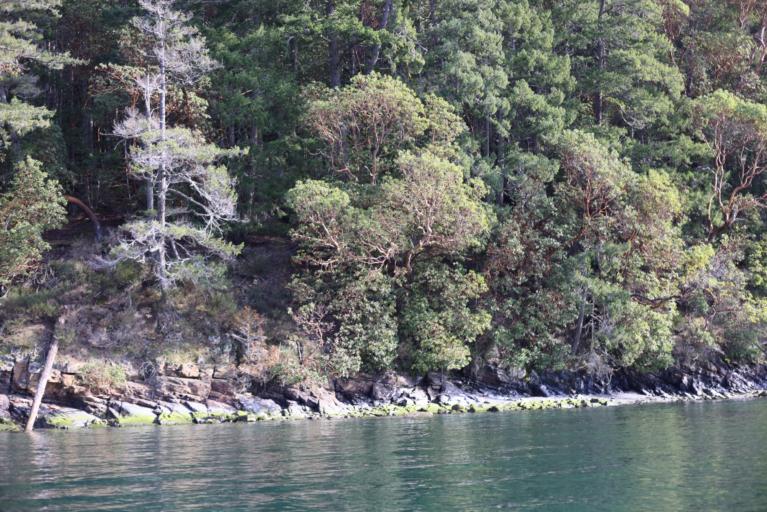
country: CA
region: British Columbia
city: Duncan
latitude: 48.7594
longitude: -123.5922
